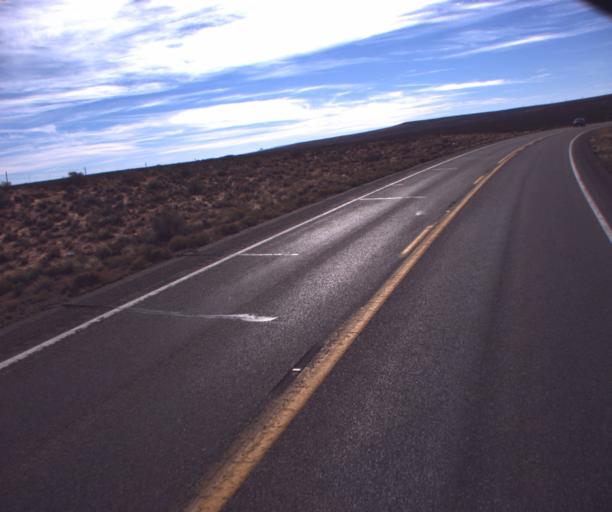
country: US
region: Arizona
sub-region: Coconino County
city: LeChee
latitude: 36.8278
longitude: -111.3102
